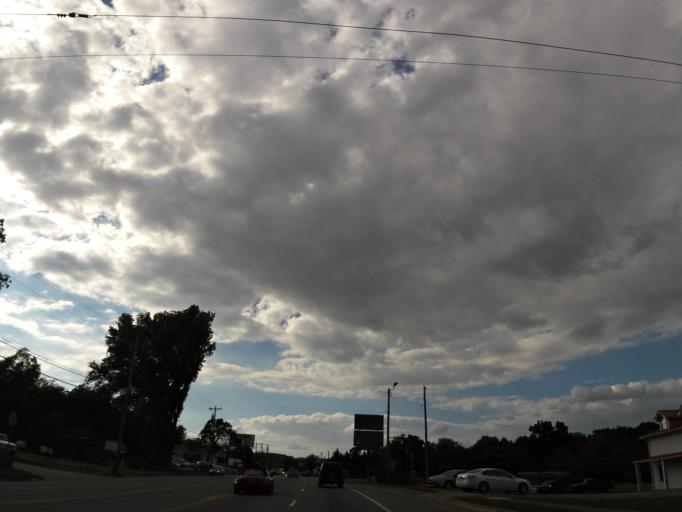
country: US
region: Georgia
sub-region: Catoosa County
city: Lakeview
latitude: 34.9662
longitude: -85.2618
